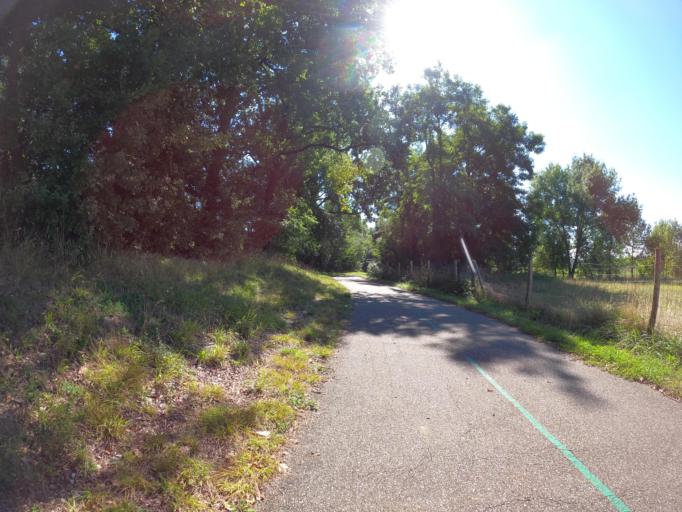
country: FR
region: Aquitaine
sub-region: Departement du Lot-et-Garonne
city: Bias
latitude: 44.4092
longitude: 0.6627
